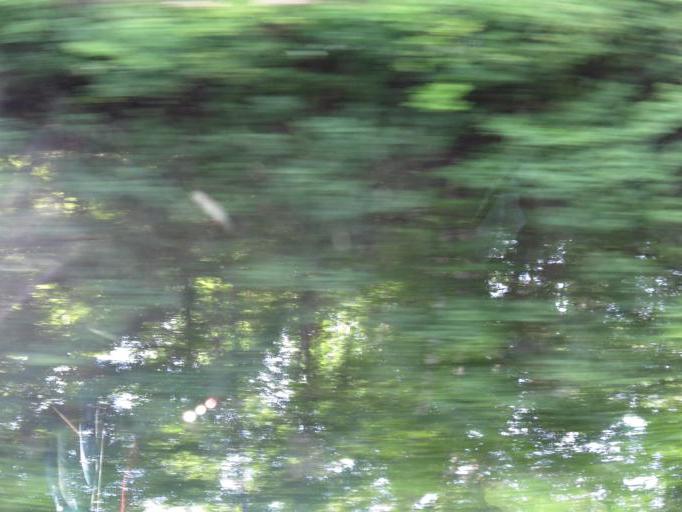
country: US
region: Tennessee
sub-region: Humphreys County
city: McEwen
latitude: 36.1056
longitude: -87.6945
